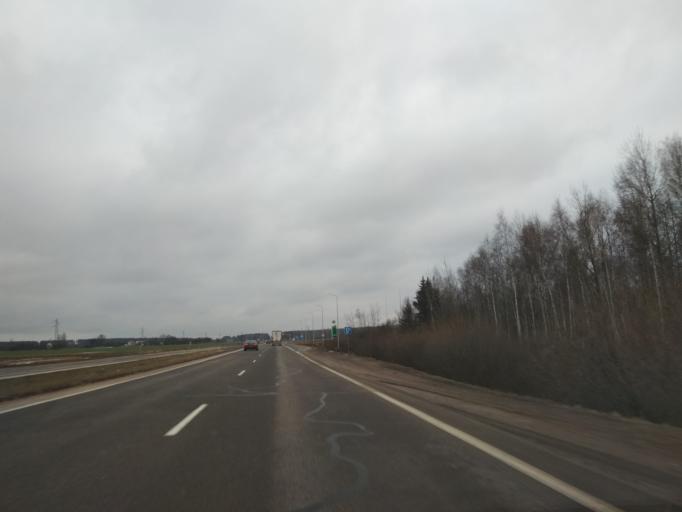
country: BY
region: Minsk
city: Dukora
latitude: 53.6355
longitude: 28.0106
